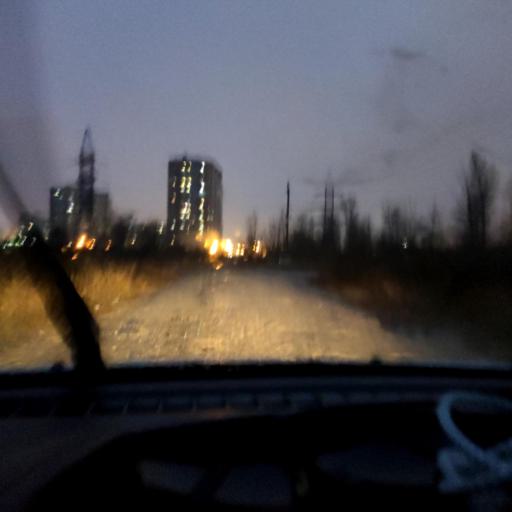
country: RU
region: Samara
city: Tol'yatti
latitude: 53.5445
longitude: 49.3946
